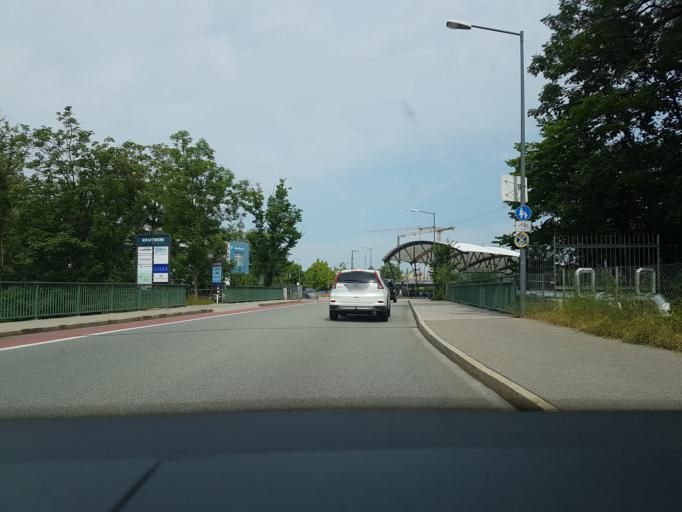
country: DE
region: Bavaria
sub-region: Upper Bavaria
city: Rosenheim
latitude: 47.8481
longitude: 12.1194
